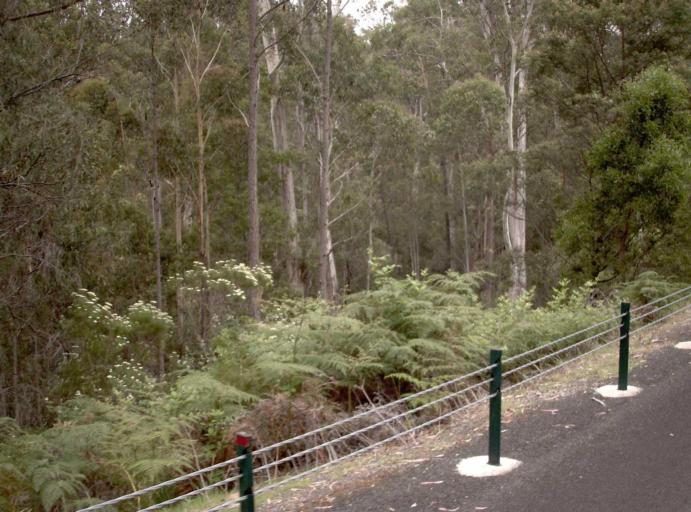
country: AU
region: New South Wales
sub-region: Bombala
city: Bombala
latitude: -37.2599
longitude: 149.2371
